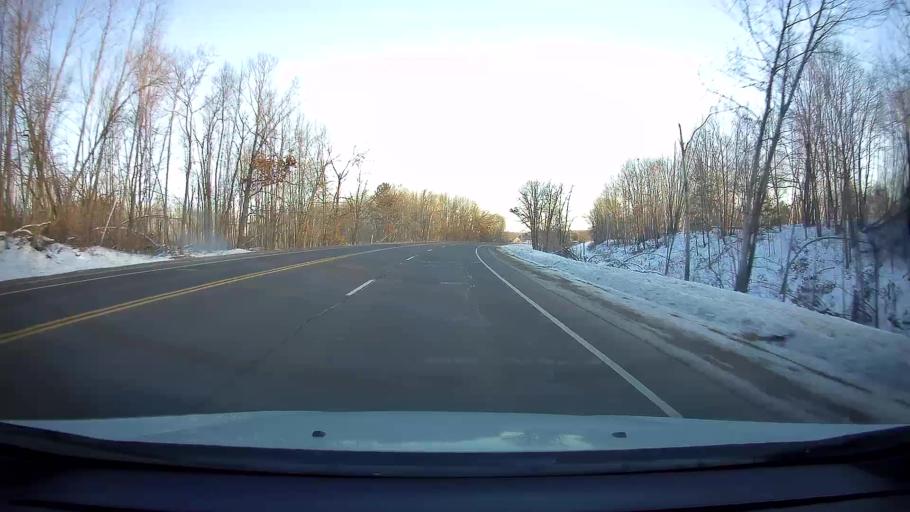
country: US
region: Wisconsin
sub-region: Barron County
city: Turtle Lake
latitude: 45.4349
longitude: -92.1299
